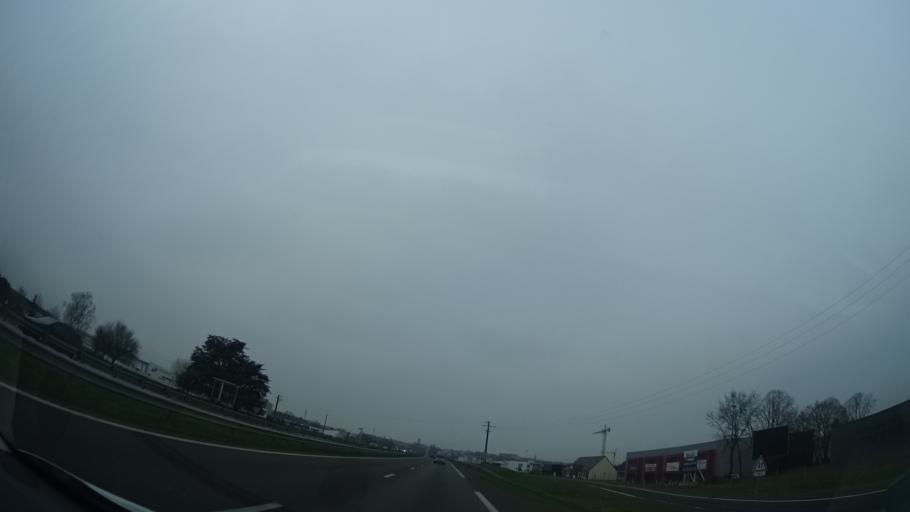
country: FR
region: Brittany
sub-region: Departement d'Ille-et-Vilaine
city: Noyal-sur-Vilaine
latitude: 48.1059
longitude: -1.5041
